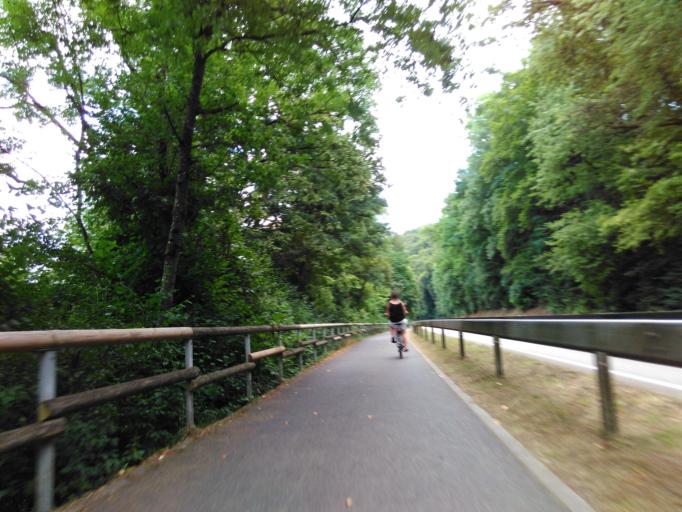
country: DE
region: Rheinland-Pfalz
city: Ralingen
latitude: 49.8131
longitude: 6.4850
